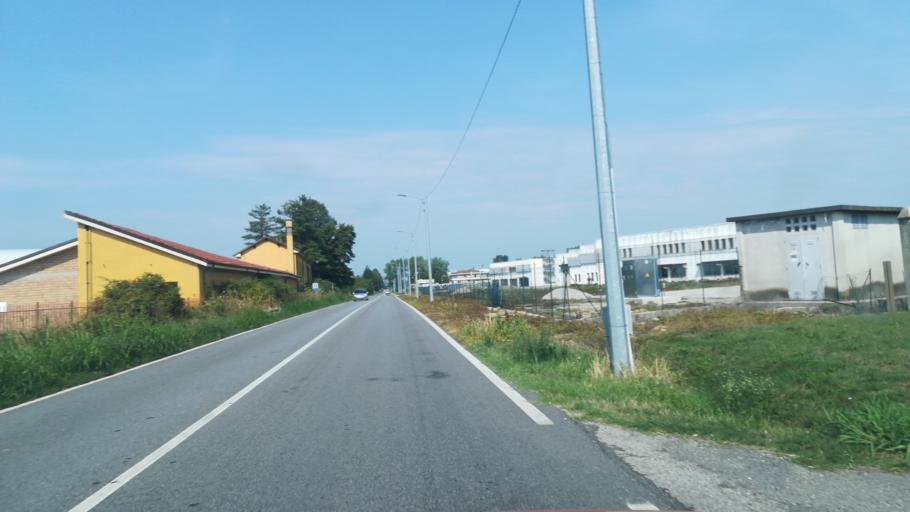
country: IT
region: Piedmont
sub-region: Provincia di Alessandria
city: Occimiano
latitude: 45.0702
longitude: 8.4925
